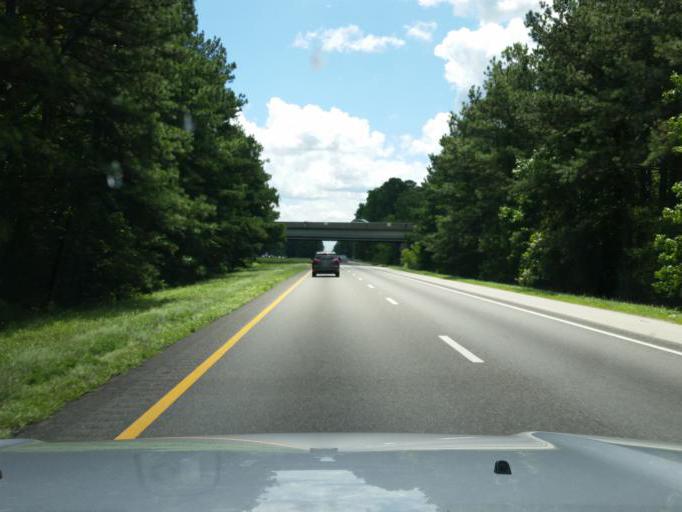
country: US
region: Virginia
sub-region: James City County
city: Williamsburg
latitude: 37.3535
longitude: -76.7326
